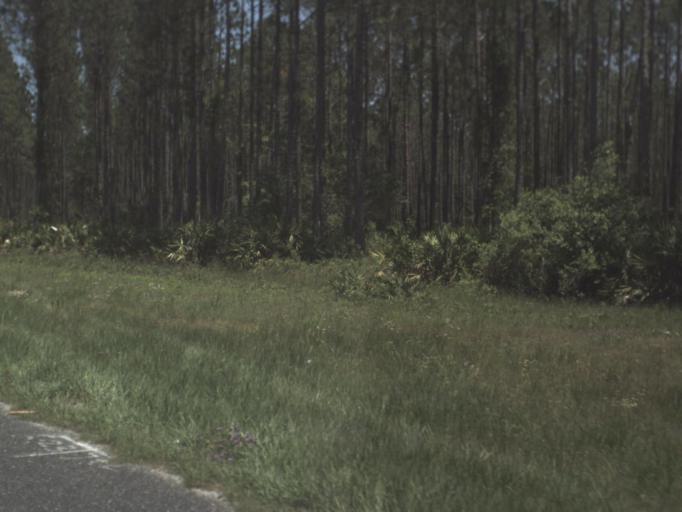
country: US
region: Florida
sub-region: Union County
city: Lake Butler
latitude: 30.2218
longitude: -82.3526
